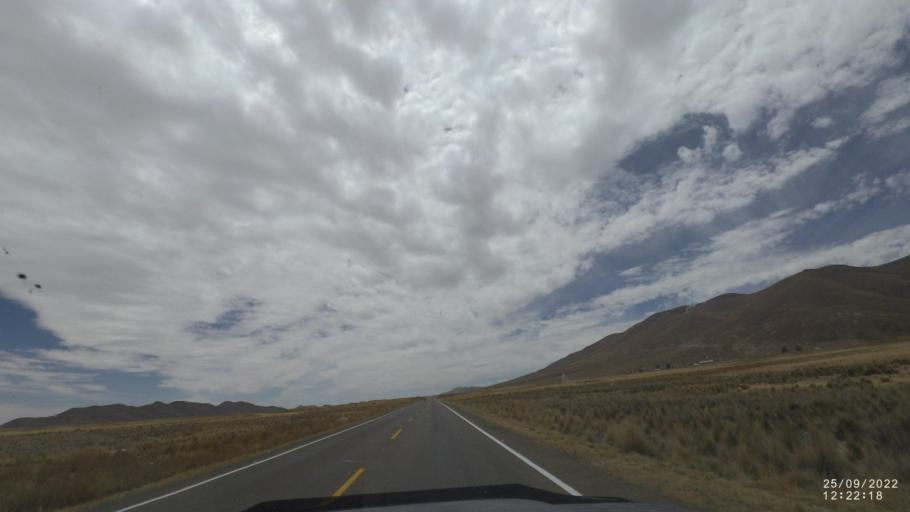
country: BO
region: Oruro
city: Poopo
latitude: -18.3945
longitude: -66.9780
